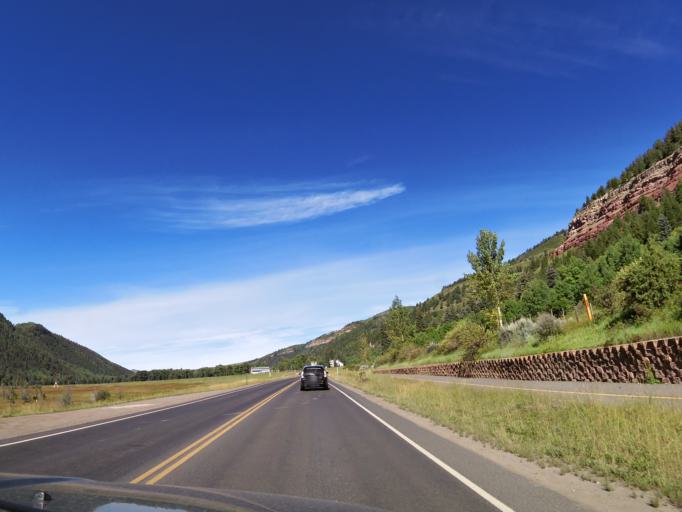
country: US
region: Colorado
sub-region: San Miguel County
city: Telluride
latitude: 37.9448
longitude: -107.8279
